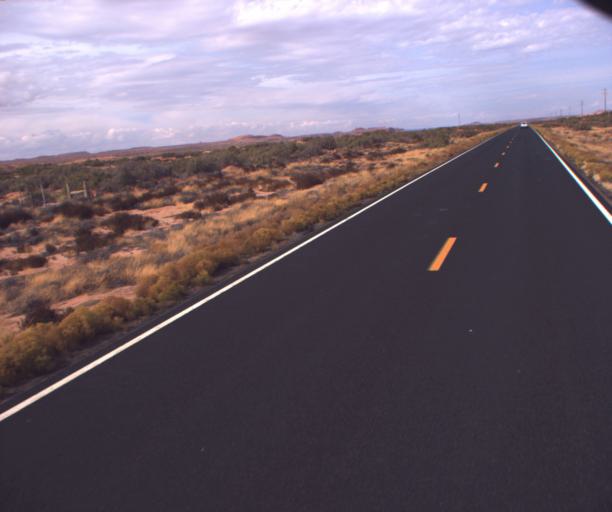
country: US
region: Arizona
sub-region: Apache County
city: Many Farms
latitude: 36.6371
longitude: -109.5873
